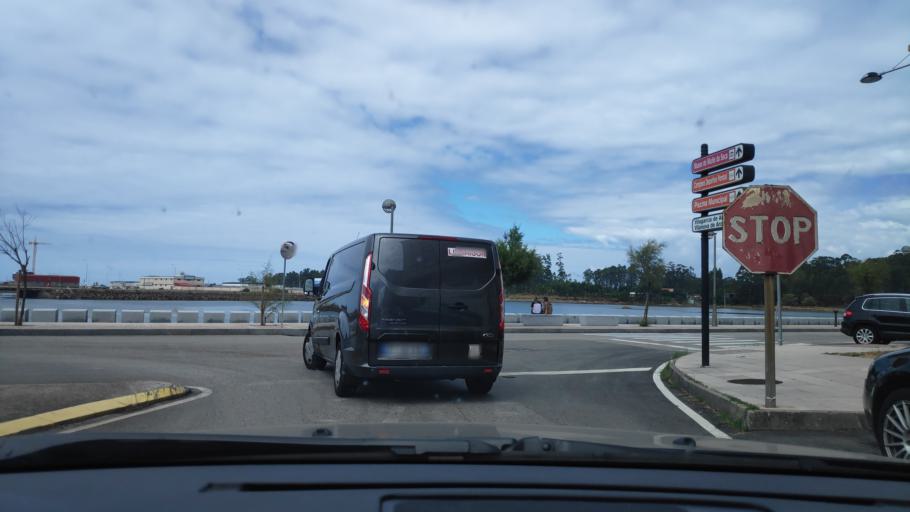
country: ES
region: Galicia
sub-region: Provincia de Pontevedra
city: Cambados
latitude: 42.5205
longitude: -8.8160
